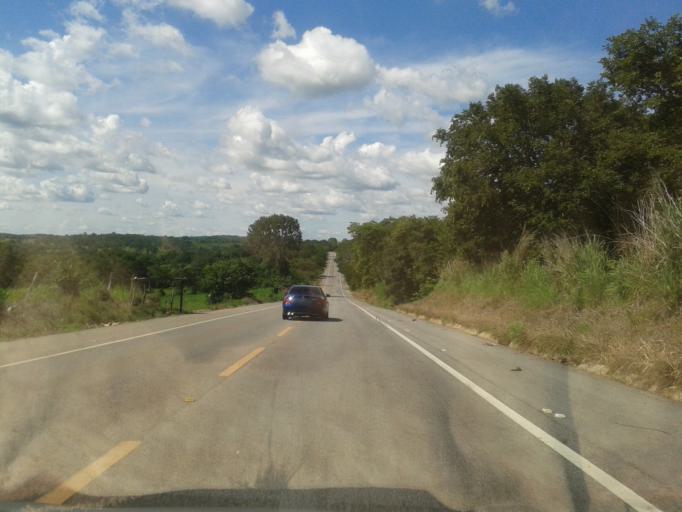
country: BR
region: Goias
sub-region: Itapuranga
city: Itapuranga
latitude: -15.6486
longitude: -50.2238
